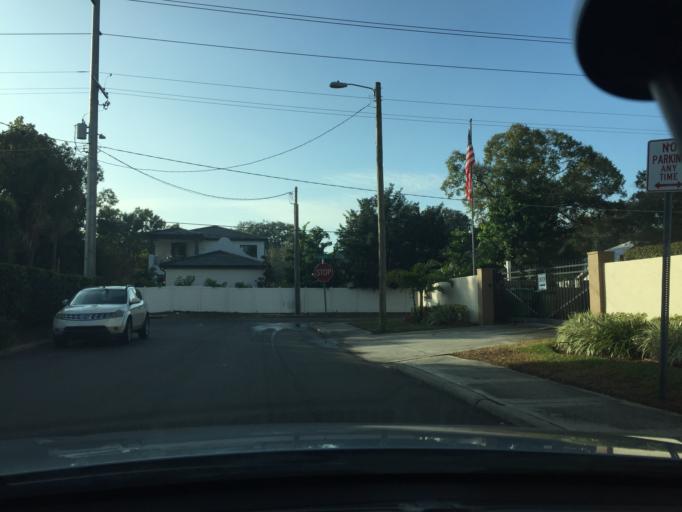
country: US
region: Florida
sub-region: Hillsborough County
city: Tampa
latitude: 27.9378
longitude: -82.4954
